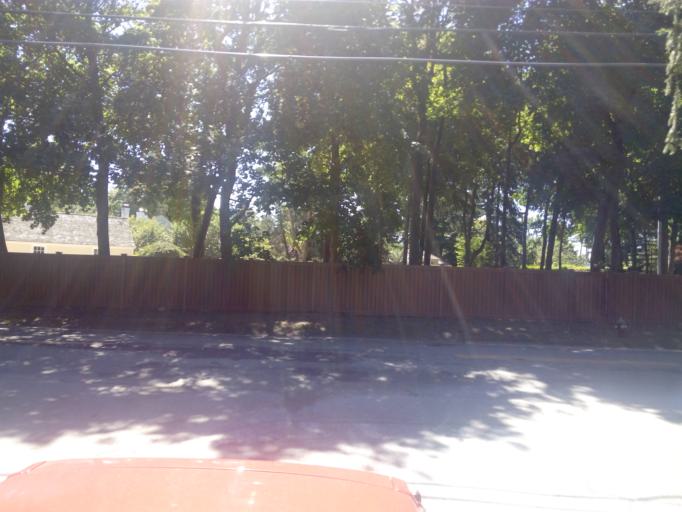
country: US
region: New York
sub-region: Nassau County
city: Upper Brookville
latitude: 40.8419
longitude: -73.5791
